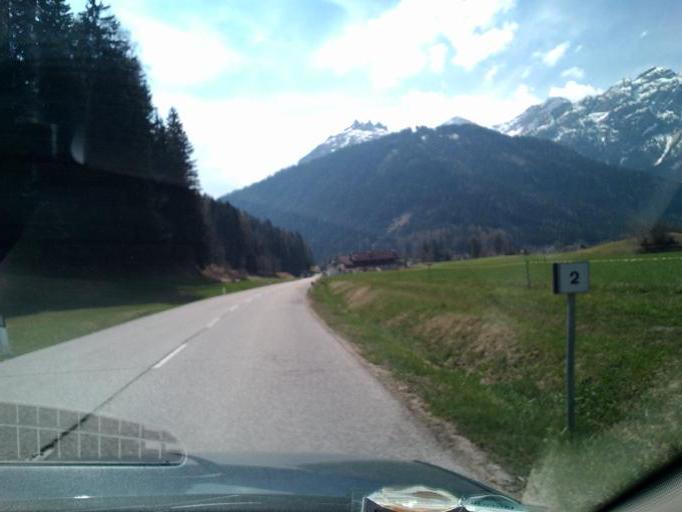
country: IT
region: Trentino-Alto Adige
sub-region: Bolzano
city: Braies
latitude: 46.7273
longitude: 12.1409
